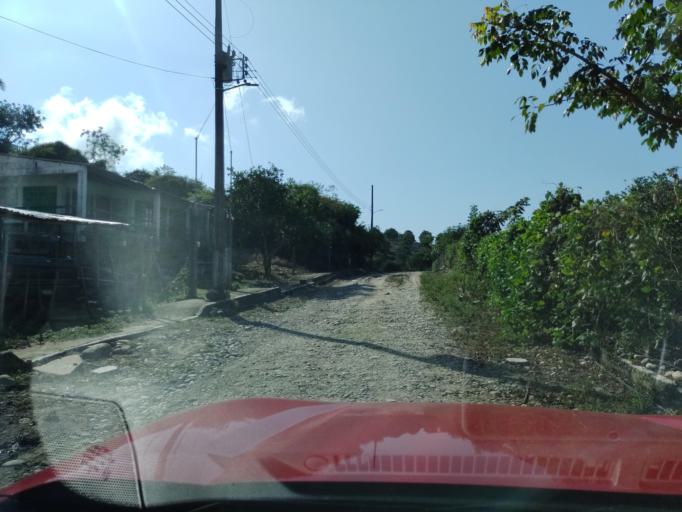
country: MX
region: Veracruz
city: Agua Dulce
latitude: 20.2868
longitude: -97.1858
